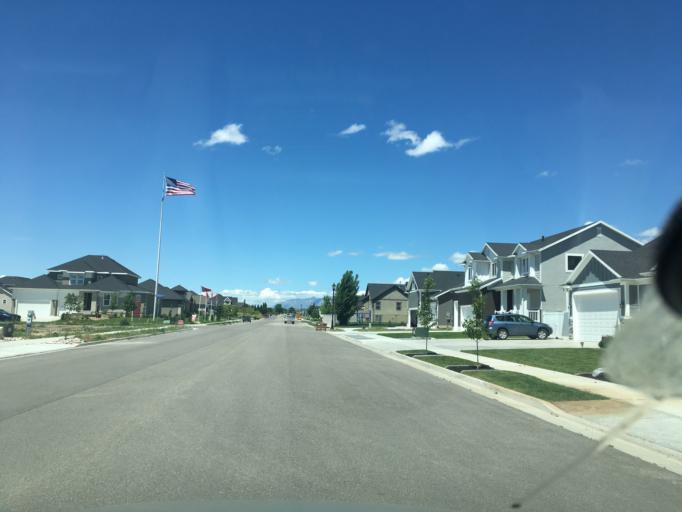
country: US
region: Utah
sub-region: Davis County
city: Layton
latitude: 41.0502
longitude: -111.9975
